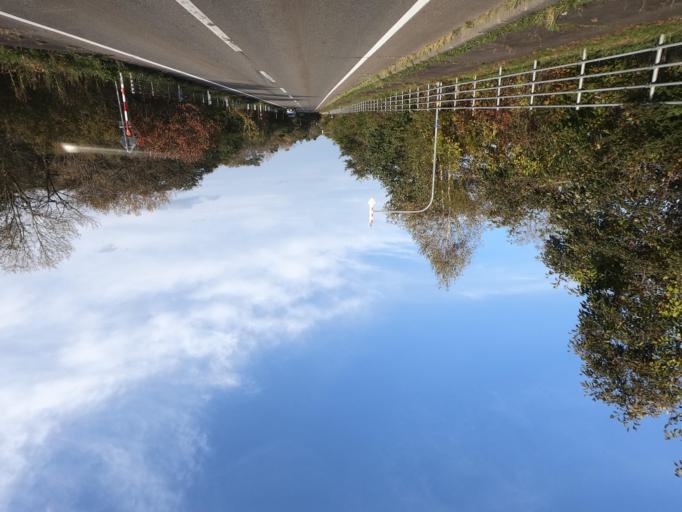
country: JP
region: Hokkaido
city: Obihiro
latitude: 42.5010
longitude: 143.4062
